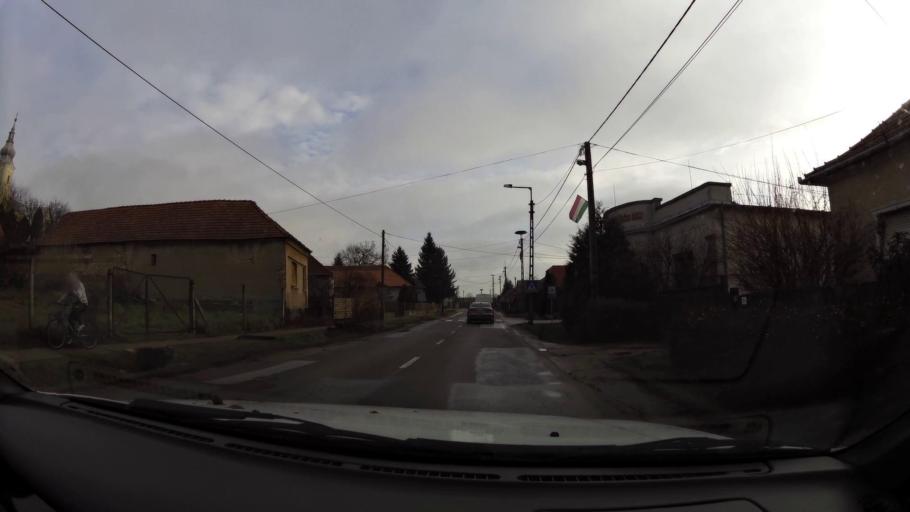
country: HU
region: Borsod-Abauj-Zemplen
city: Mucsony
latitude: 48.2699
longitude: 20.6796
